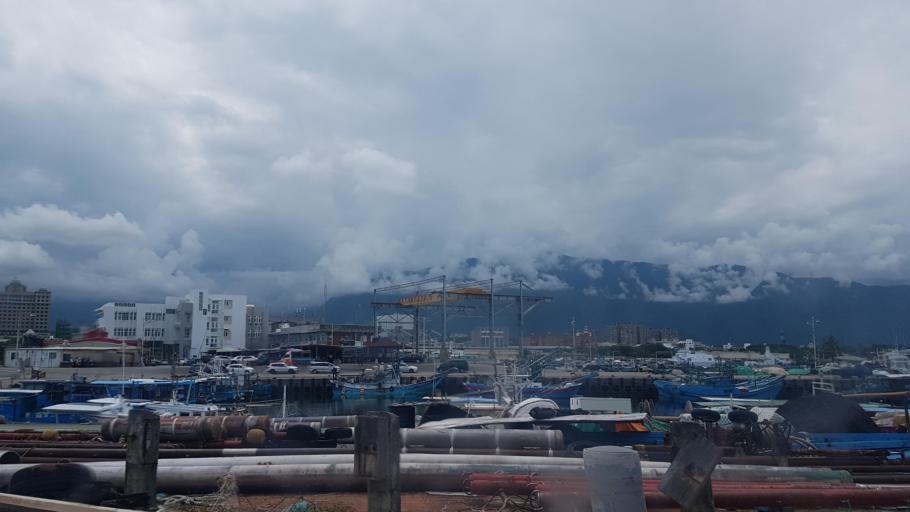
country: TW
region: Taiwan
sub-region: Hualien
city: Hualian
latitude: 23.9963
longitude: 121.6401
